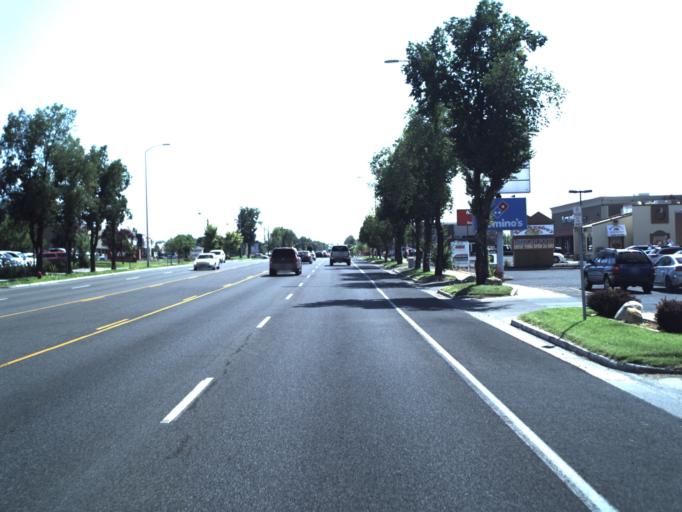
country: US
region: Utah
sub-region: Cache County
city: Logan
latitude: 41.7538
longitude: -111.8345
